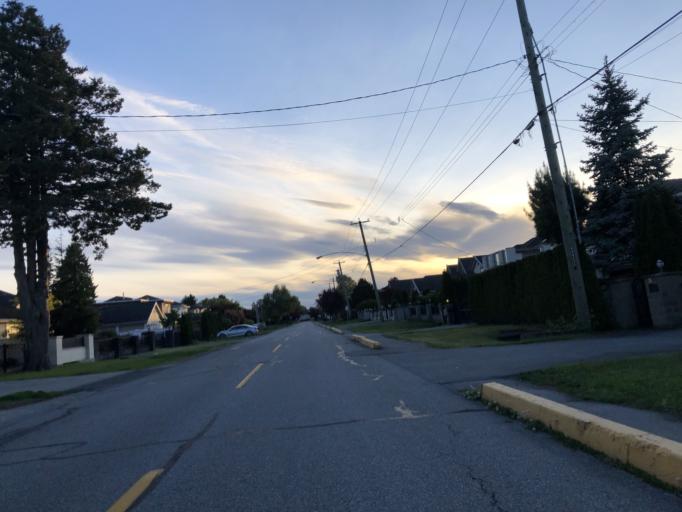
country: CA
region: British Columbia
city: Richmond
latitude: 49.1432
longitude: -123.1170
